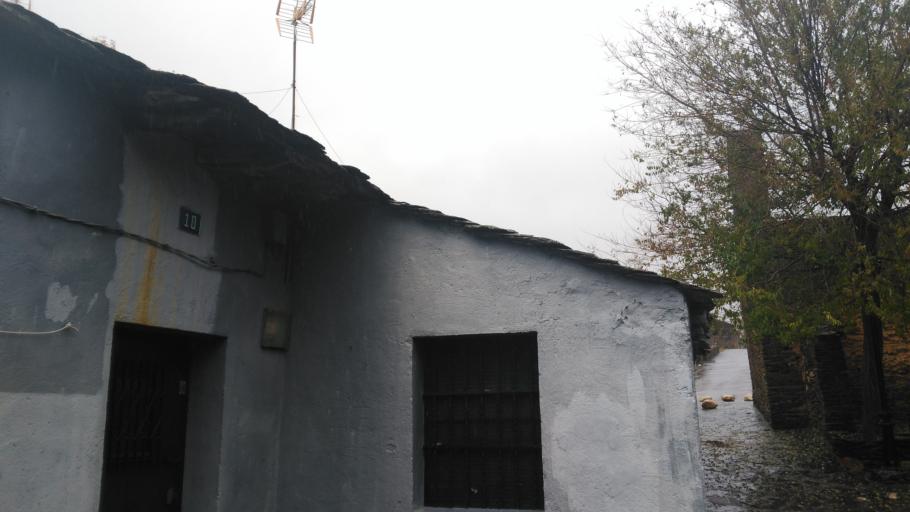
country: ES
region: Castille-La Mancha
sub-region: Provincia de Guadalajara
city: Campillo de Ranas
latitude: 41.0743
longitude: -3.3259
